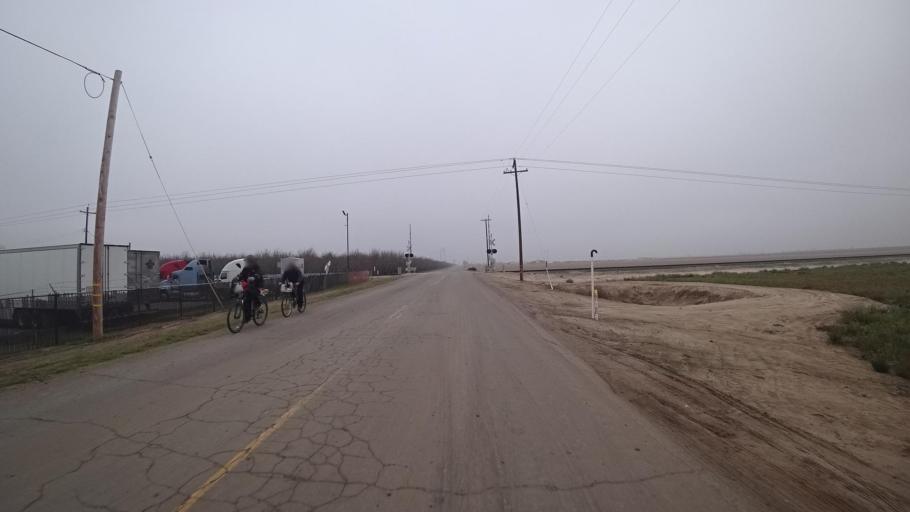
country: US
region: California
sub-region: Kern County
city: Greenfield
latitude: 35.2380
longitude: -119.1005
